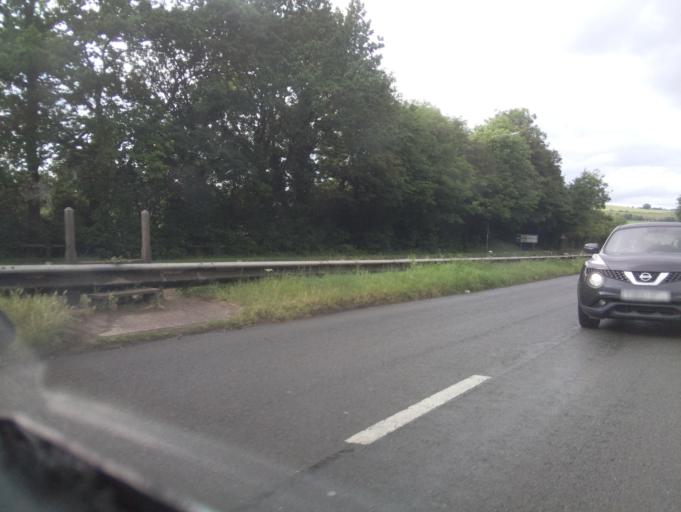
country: GB
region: England
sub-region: Dudley
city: Kingswinford
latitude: 52.5349
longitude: -2.1775
